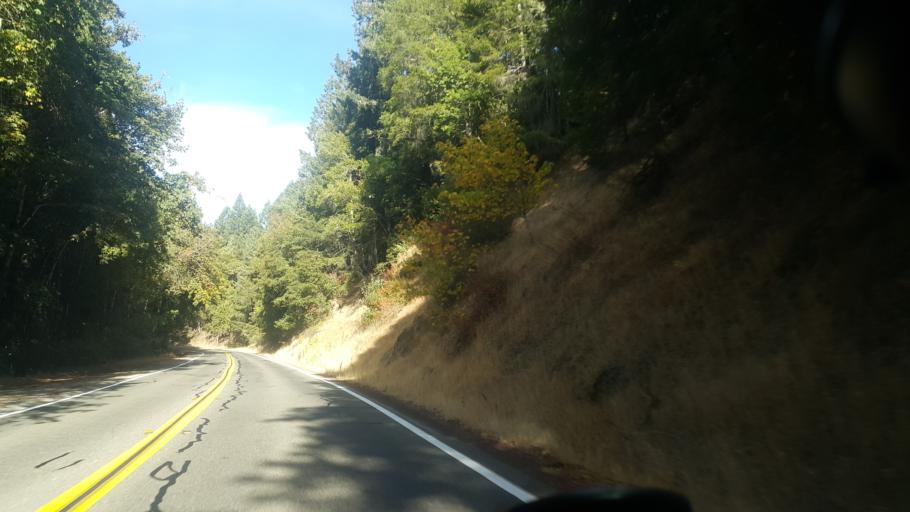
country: US
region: California
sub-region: Mendocino County
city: Brooktrails
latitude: 39.3879
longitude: -123.4375
